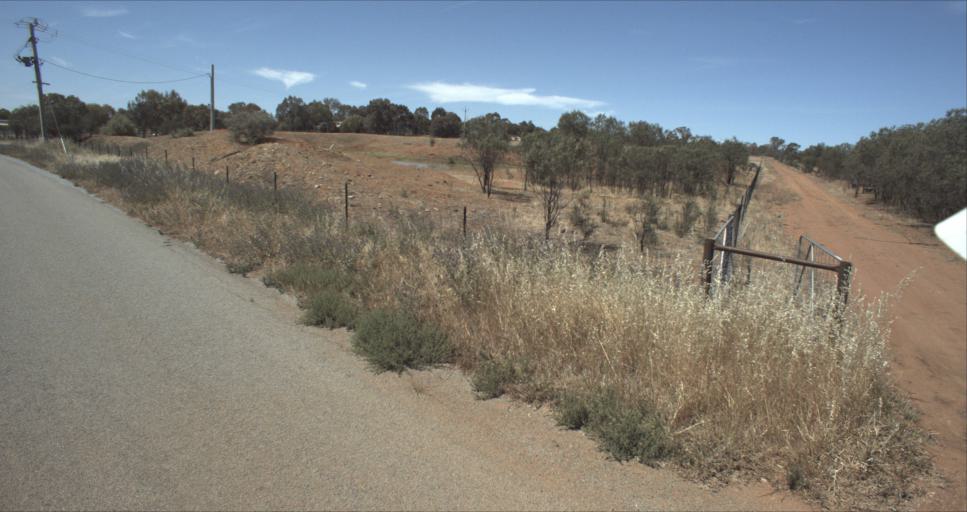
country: AU
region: New South Wales
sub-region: Leeton
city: Leeton
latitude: -34.5804
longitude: 146.4316
